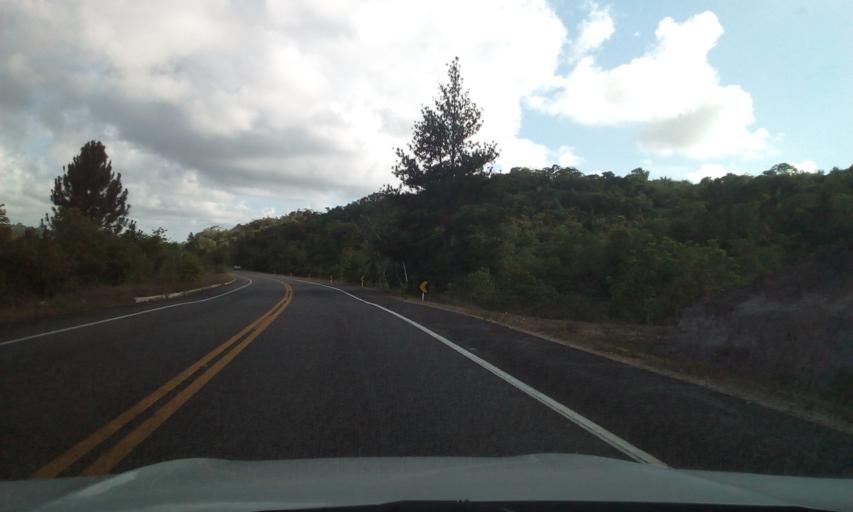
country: BR
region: Bahia
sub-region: Conde
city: Conde
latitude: -12.0733
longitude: -37.7507
